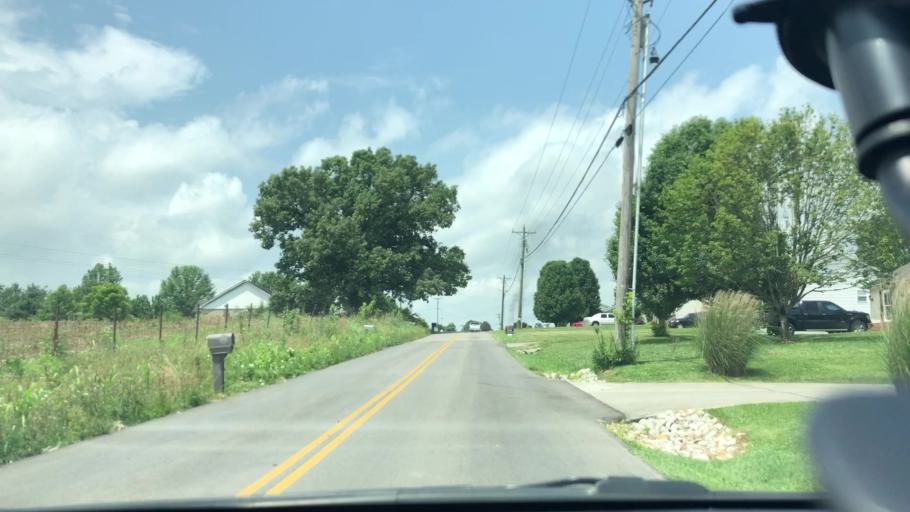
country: US
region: Kentucky
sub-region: Pulaski County
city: Somerset
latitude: 37.0595
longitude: -84.6675
